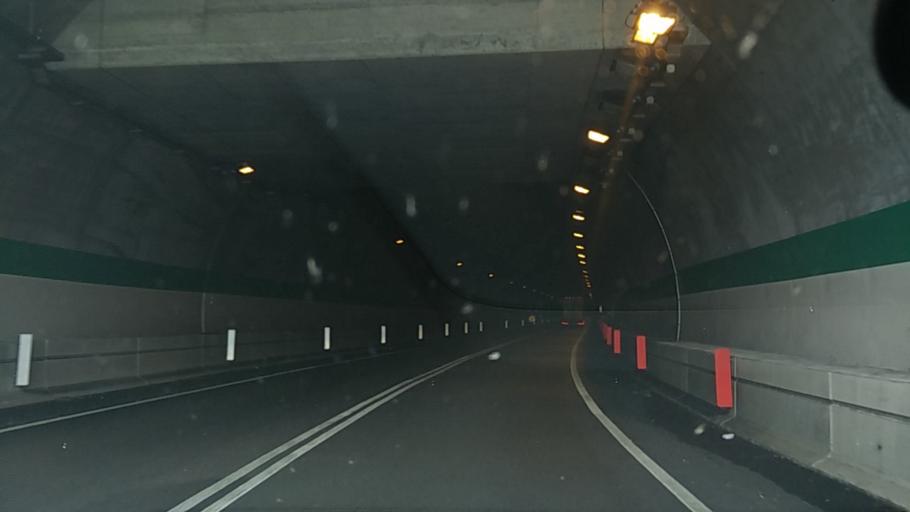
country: IT
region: Veneto
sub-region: Provincia di Belluno
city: Castion
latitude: 46.1336
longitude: 12.2276
